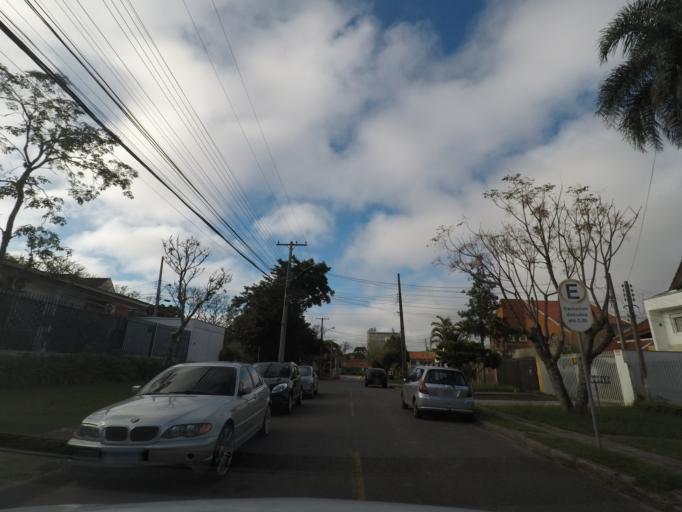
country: BR
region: Parana
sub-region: Curitiba
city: Curitiba
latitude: -25.4549
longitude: -49.2405
